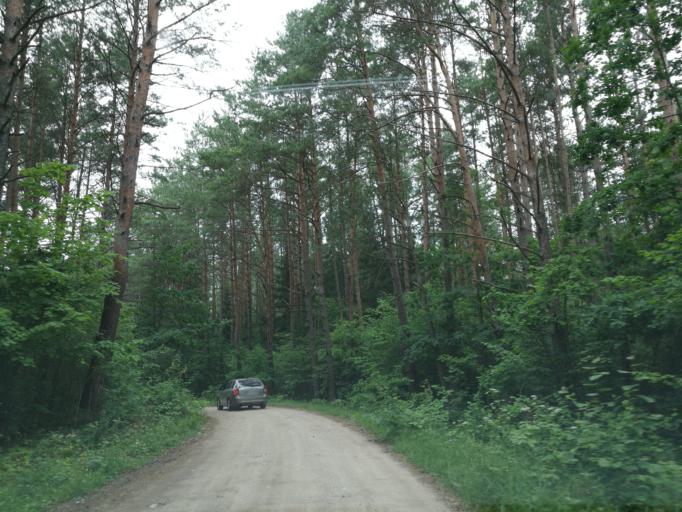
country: LT
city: Trakai
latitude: 54.6486
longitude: 24.9637
